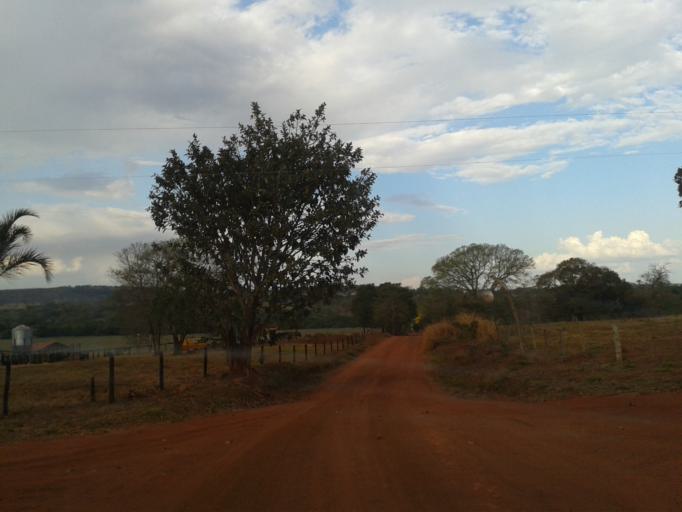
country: BR
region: Minas Gerais
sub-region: Ituiutaba
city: Ituiutaba
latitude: -19.1980
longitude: -49.8326
